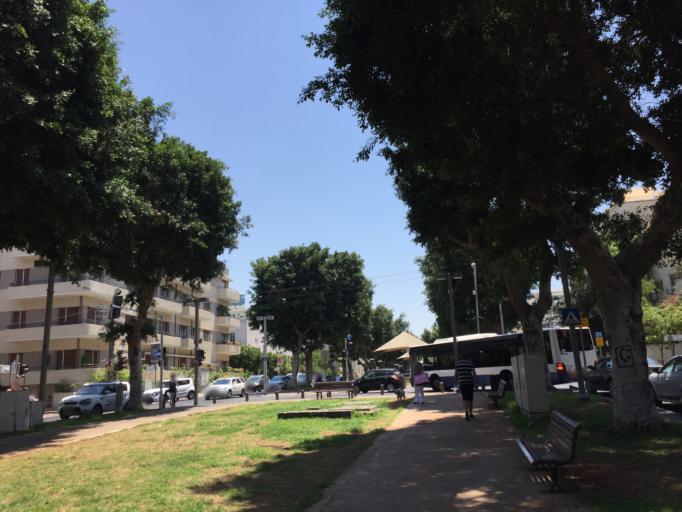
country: IL
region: Tel Aviv
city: Tel Aviv
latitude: 32.0709
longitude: 34.7789
